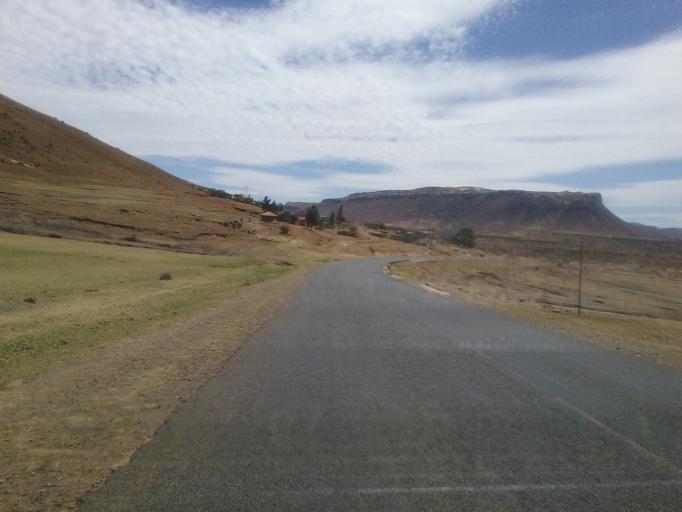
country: LS
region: Mafeteng
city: Mafeteng
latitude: -29.9096
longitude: 27.2496
